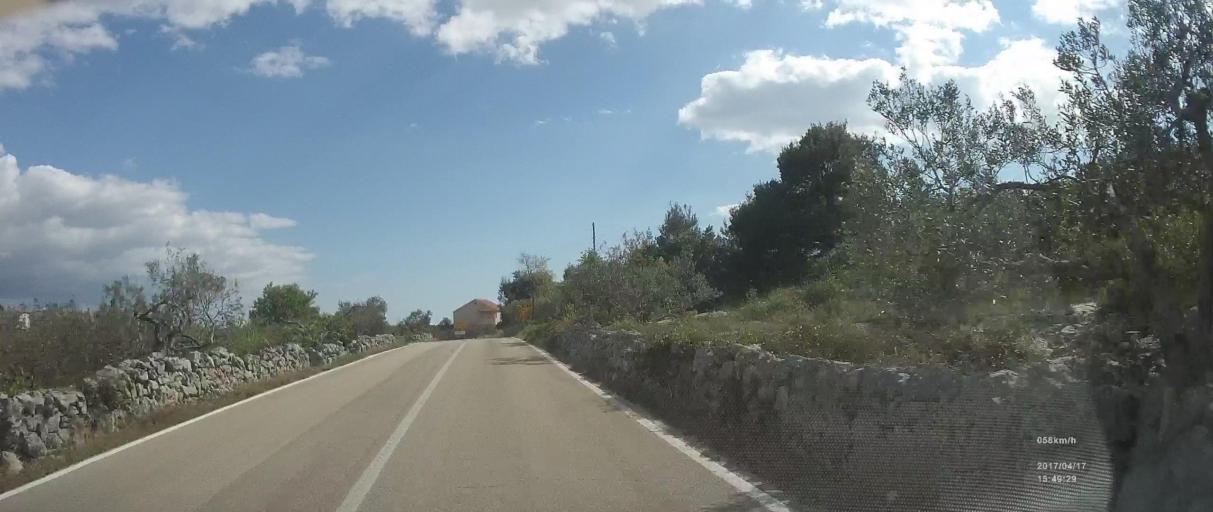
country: HR
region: Sibensko-Kniniska
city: Primosten
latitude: 43.6135
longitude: 15.9762
